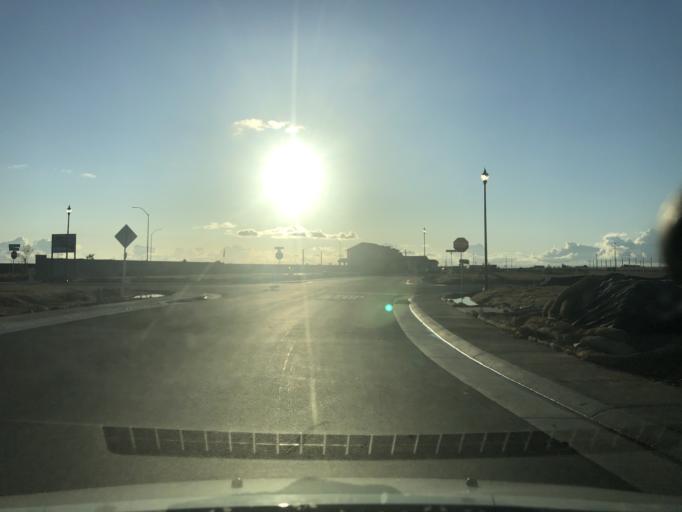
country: US
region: California
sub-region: Sacramento County
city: Antelope
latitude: 38.7603
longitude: -121.3656
